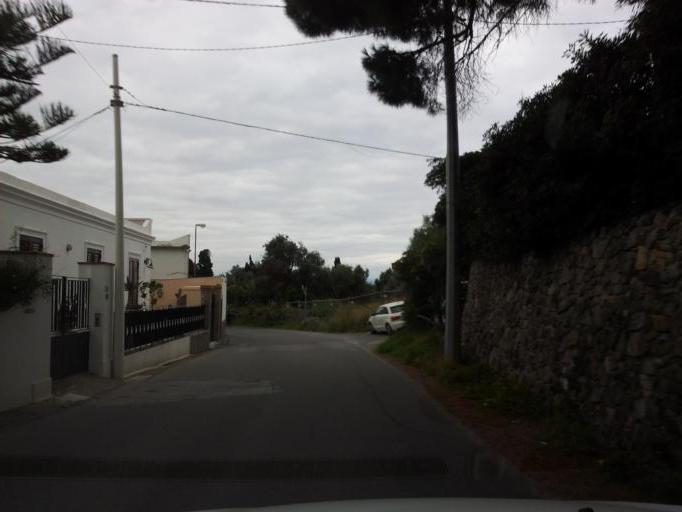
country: IT
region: Sicily
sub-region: Messina
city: Milazzo
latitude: 38.2395
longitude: 15.2461
